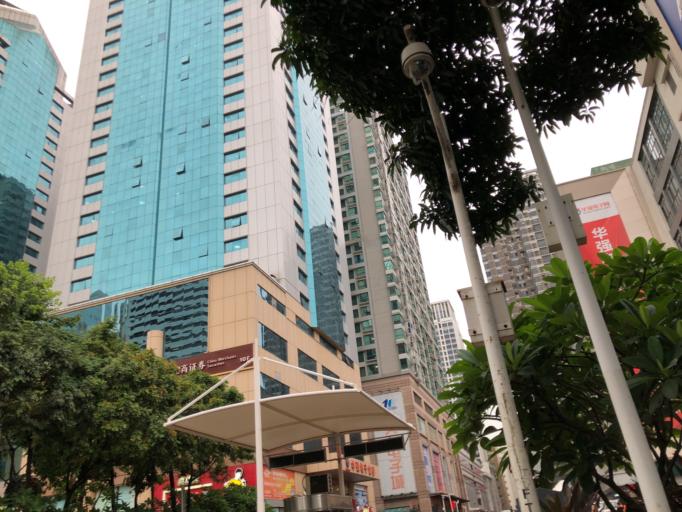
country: CN
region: Guangdong
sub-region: Shenzhen
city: Shenzhen
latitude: 22.5433
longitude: 114.0805
